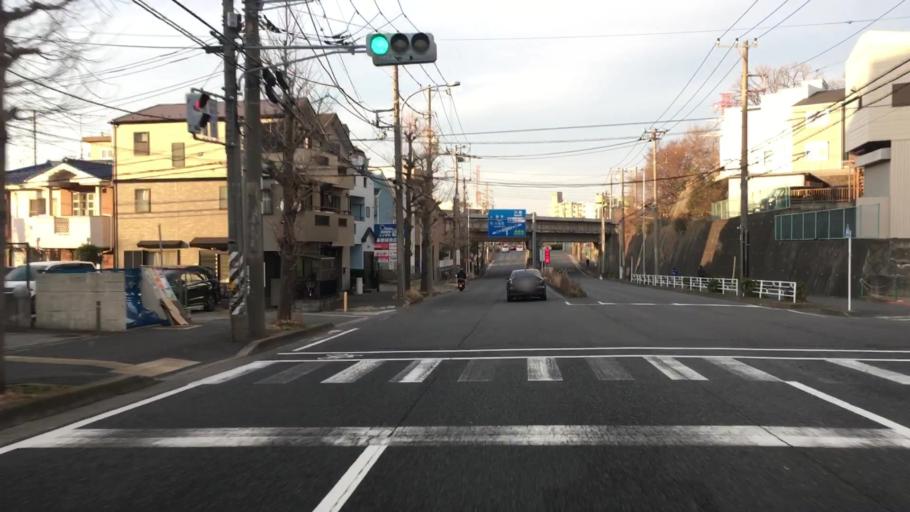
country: JP
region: Kanagawa
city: Yokohama
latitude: 35.4978
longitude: 139.6075
